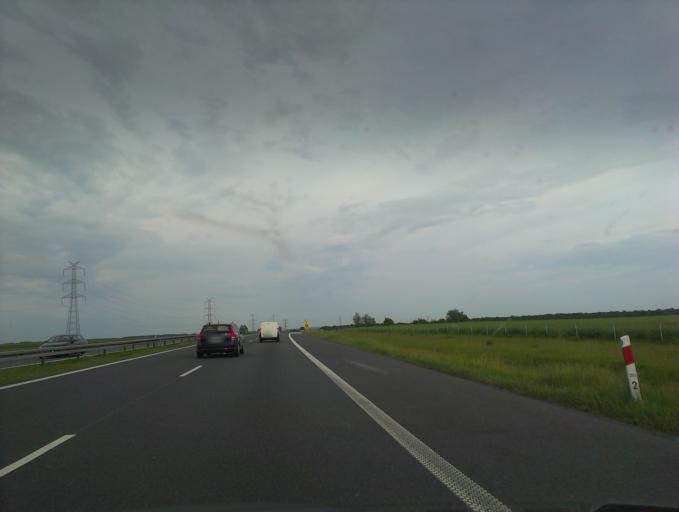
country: PL
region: Opole Voivodeship
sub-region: Powiat brzeski
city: Olszanka
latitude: 50.7362
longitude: 17.4857
